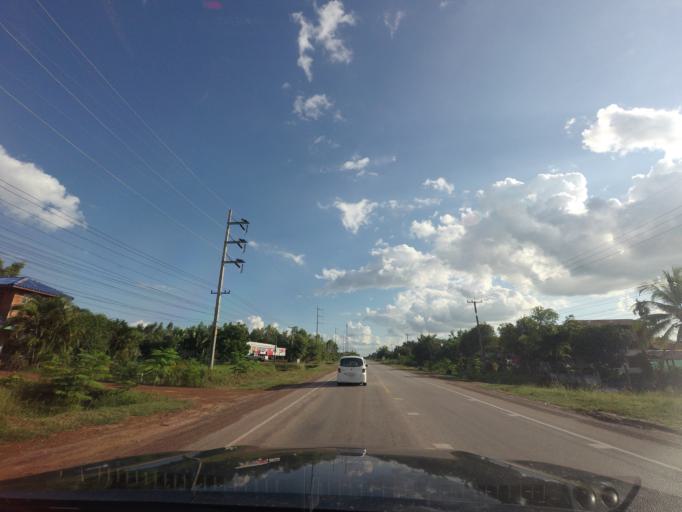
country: TH
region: Changwat Udon Thani
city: Thung Fon
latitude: 17.4862
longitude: 103.1966
